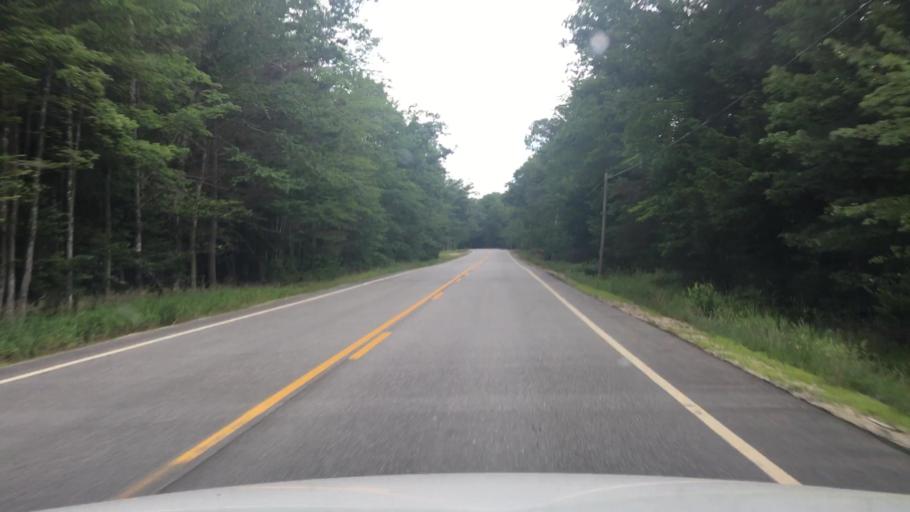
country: US
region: Maine
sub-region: Oxford County
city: Hartford
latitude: 44.3730
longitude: -70.4027
